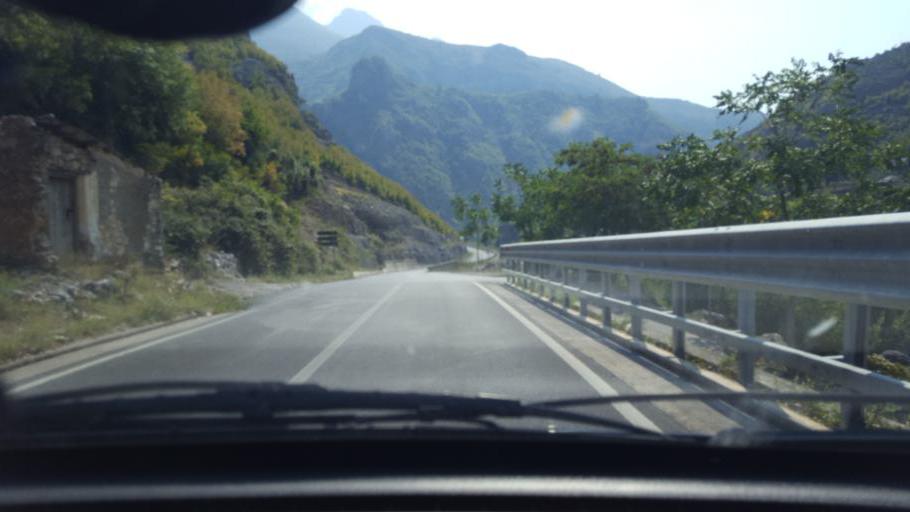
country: AL
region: Shkoder
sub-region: Rrethi i Malesia e Madhe
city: Kastrat
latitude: 42.4614
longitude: 19.5613
